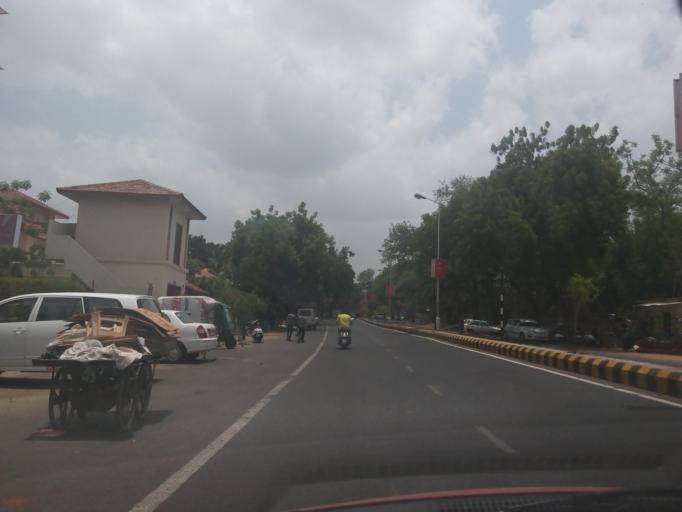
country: IN
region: Gujarat
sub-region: Ahmadabad
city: Sarkhej
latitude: 23.0437
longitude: 72.5201
